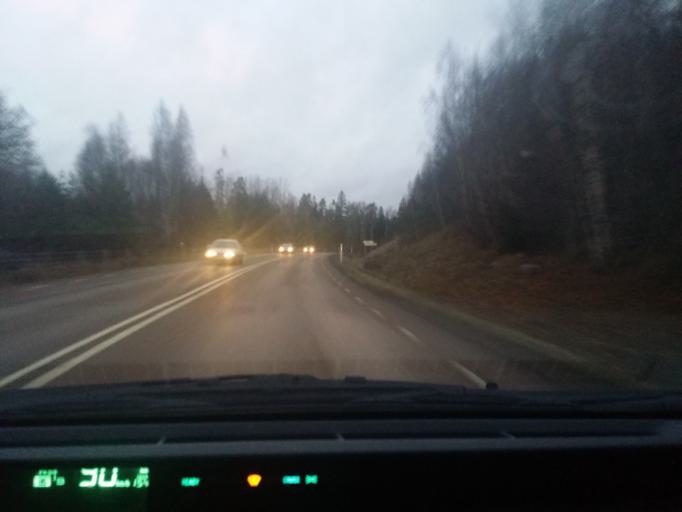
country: SE
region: Soedermanland
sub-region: Eskilstuna Kommun
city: Kvicksund
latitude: 59.5302
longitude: 16.3212
